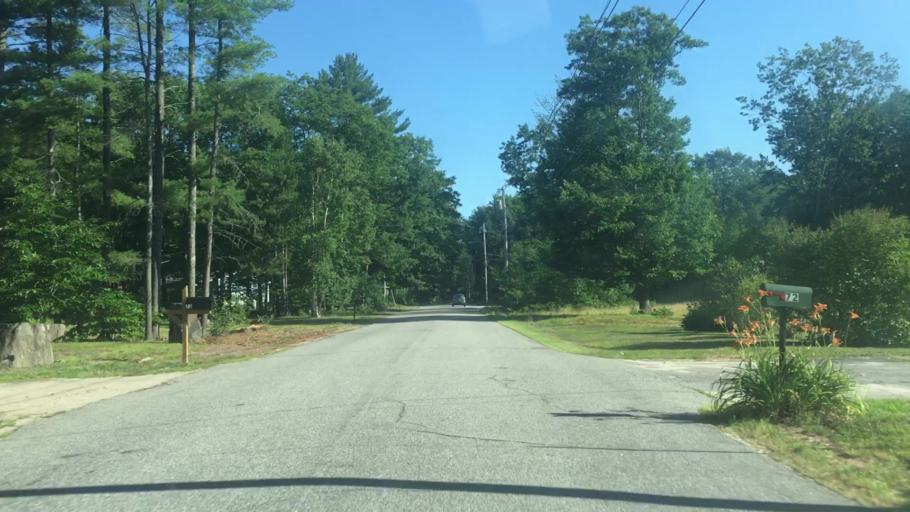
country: US
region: Maine
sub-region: Cumberland County
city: Gorham
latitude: 43.7234
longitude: -70.5158
